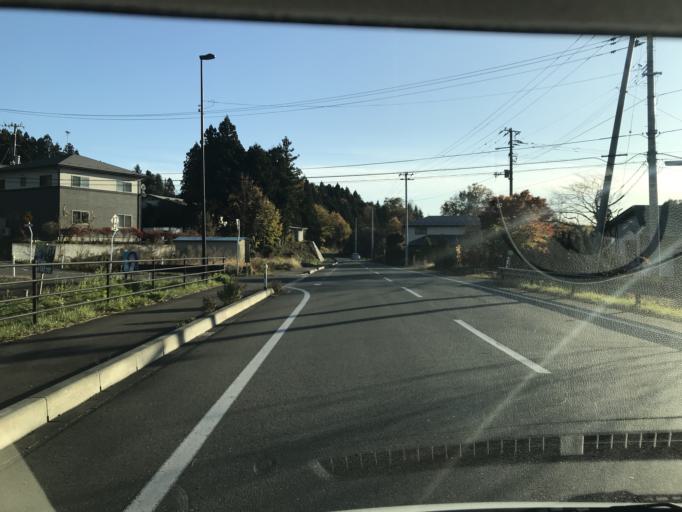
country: JP
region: Iwate
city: Mizusawa
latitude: 39.1248
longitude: 141.1881
